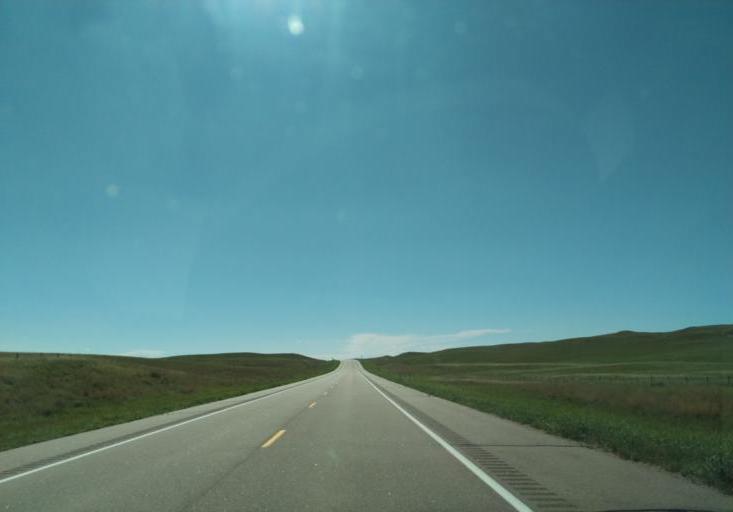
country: US
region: South Dakota
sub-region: Bennett County
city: Martin
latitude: 42.9407
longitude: -101.3431
